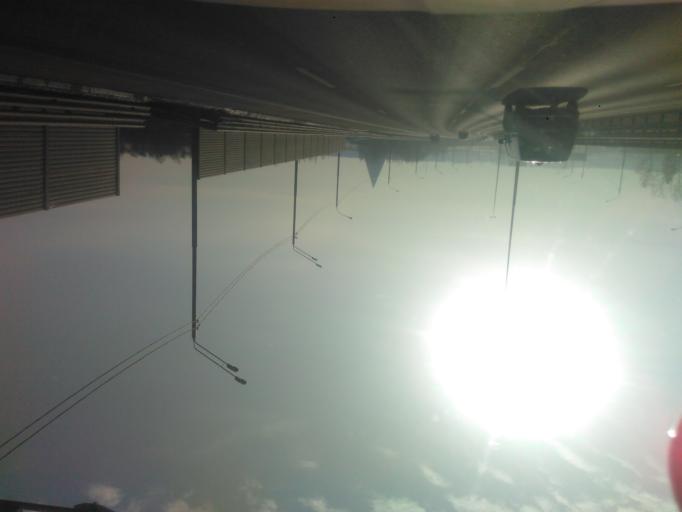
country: RU
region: Moskovskaya
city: Pavlovskaya Sloboda
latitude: 55.7893
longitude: 37.0576
